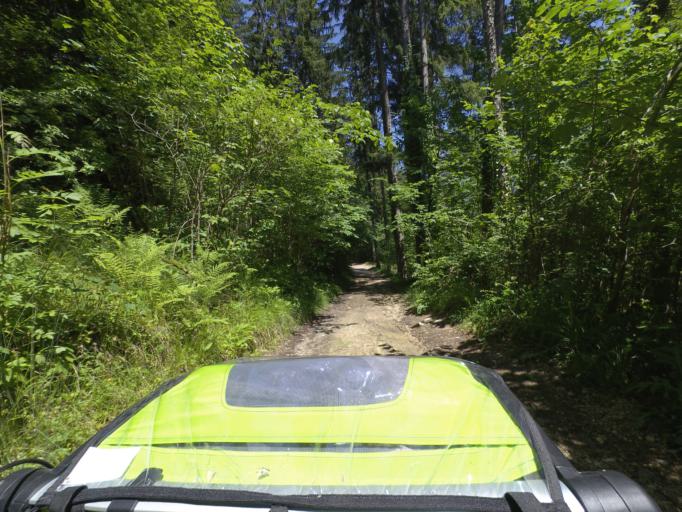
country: DE
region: Bavaria
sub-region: Upper Bavaria
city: Bayerisch Gmain
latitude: 47.7217
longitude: 12.9298
